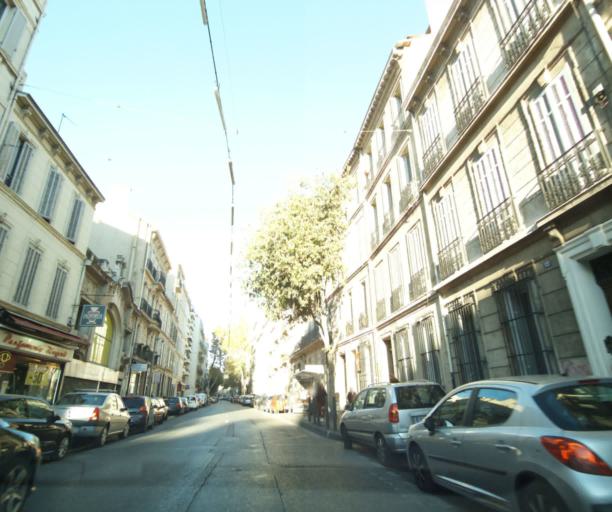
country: FR
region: Provence-Alpes-Cote d'Azur
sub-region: Departement des Bouches-du-Rhone
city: Marseille 04
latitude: 43.3031
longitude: 5.3973
